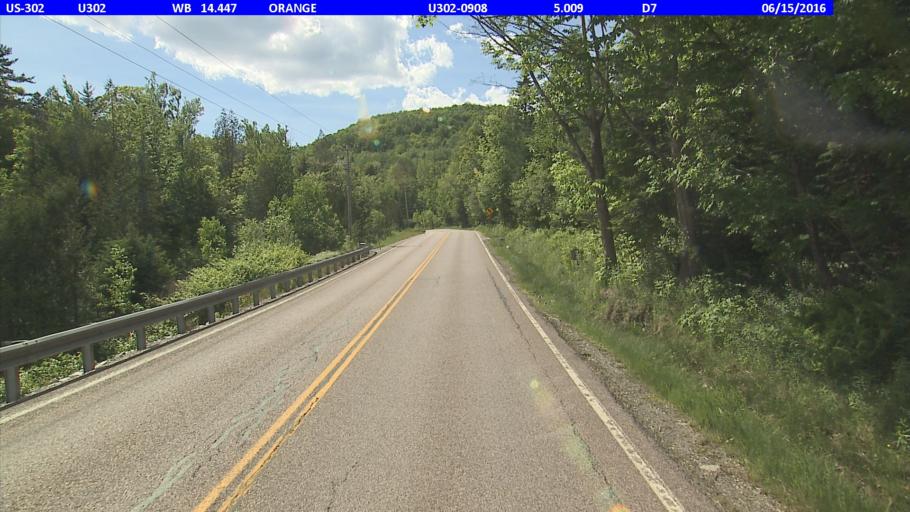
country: US
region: Vermont
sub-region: Washington County
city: South Barre
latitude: 44.1424
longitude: -72.3411
